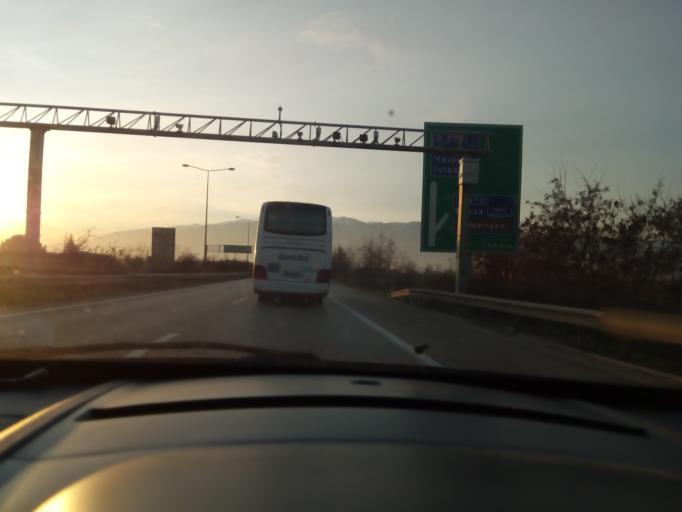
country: TR
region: Bursa
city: Demirtas
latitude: 40.2776
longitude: 29.0444
